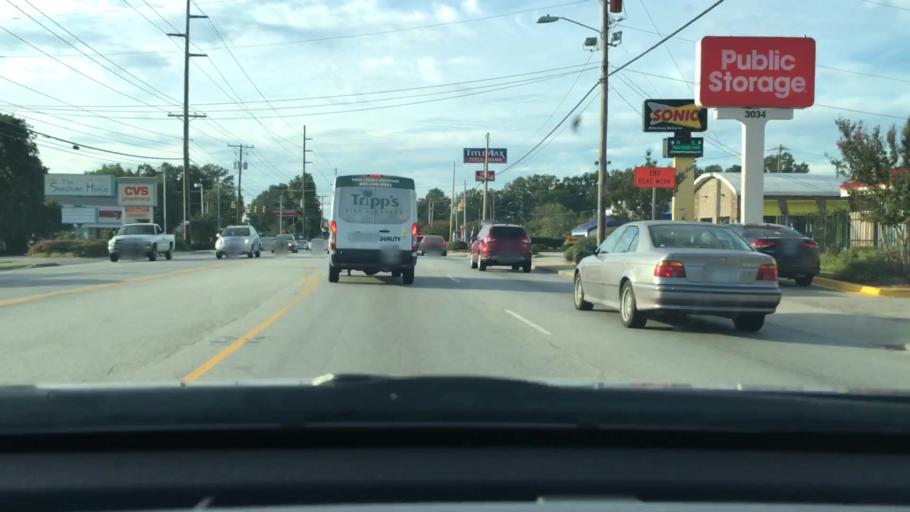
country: US
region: South Carolina
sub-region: Lexington County
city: Saint Andrews
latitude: 34.0491
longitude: -81.1047
